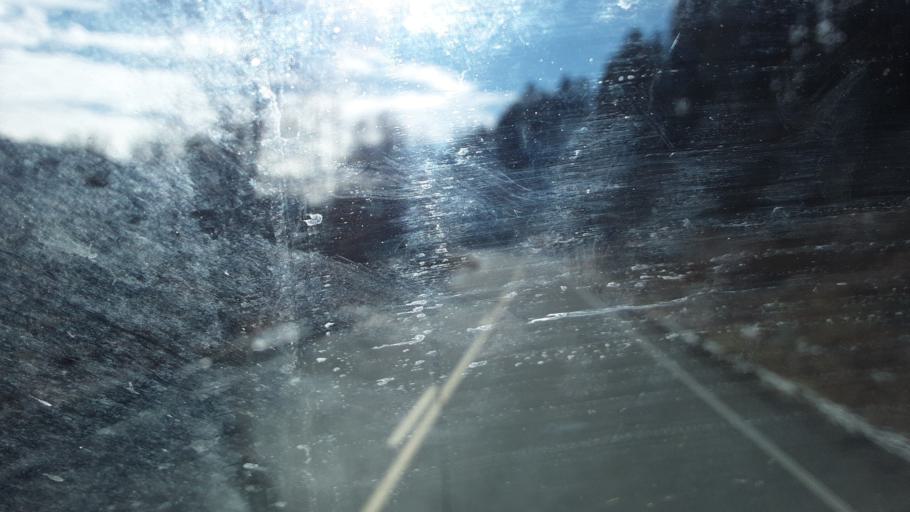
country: US
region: Colorado
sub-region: La Plata County
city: Bayfield
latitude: 37.3507
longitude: -107.6943
